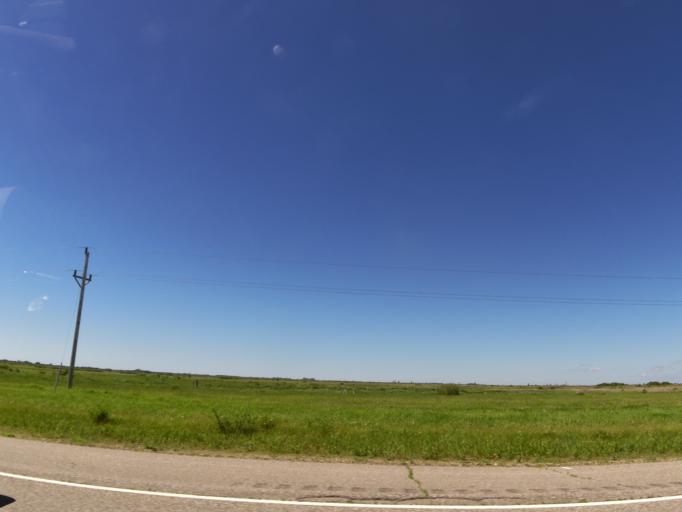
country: US
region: Minnesota
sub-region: Red Lake County
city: Red Lake Falls
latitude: 47.7350
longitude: -96.2118
